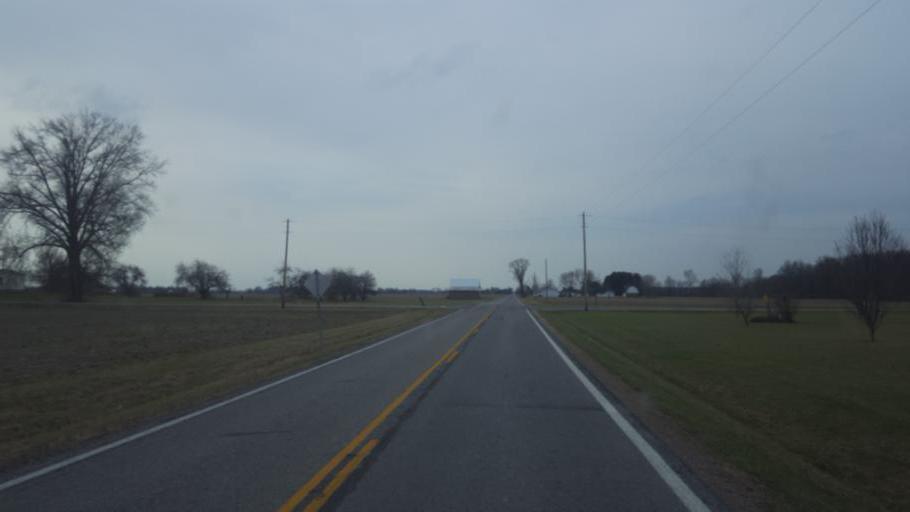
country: US
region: Ohio
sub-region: Morrow County
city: Cardington
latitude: 40.6170
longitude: -82.9625
